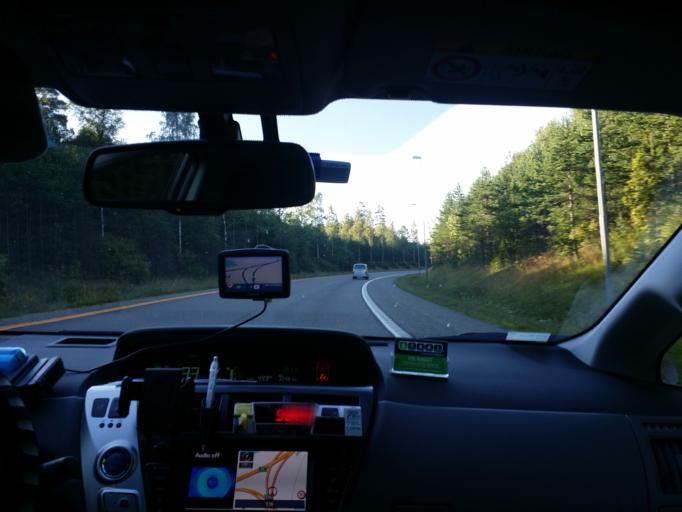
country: NO
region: Akershus
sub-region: Ullensaker
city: Jessheim
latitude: 60.1592
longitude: 11.1479
